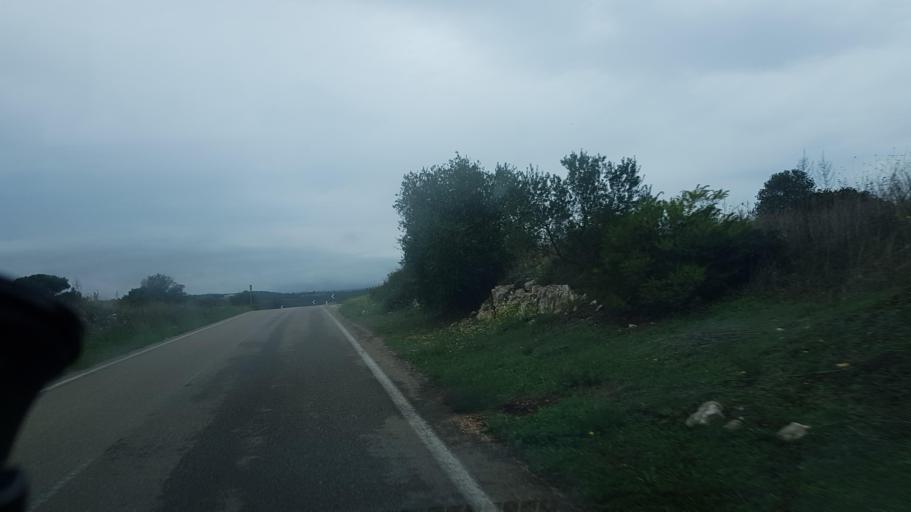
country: IT
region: Apulia
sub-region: Provincia di Brindisi
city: Ostuni
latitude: 40.7391
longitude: 17.5439
